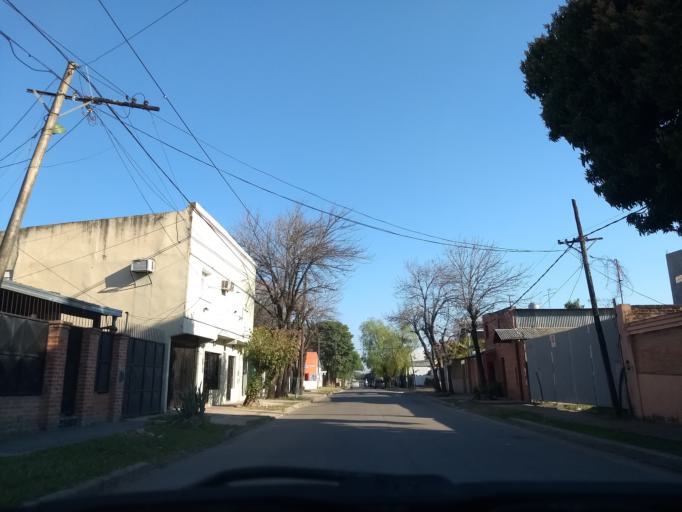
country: AR
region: Corrientes
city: Corrientes
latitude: -27.4743
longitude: -58.8066
